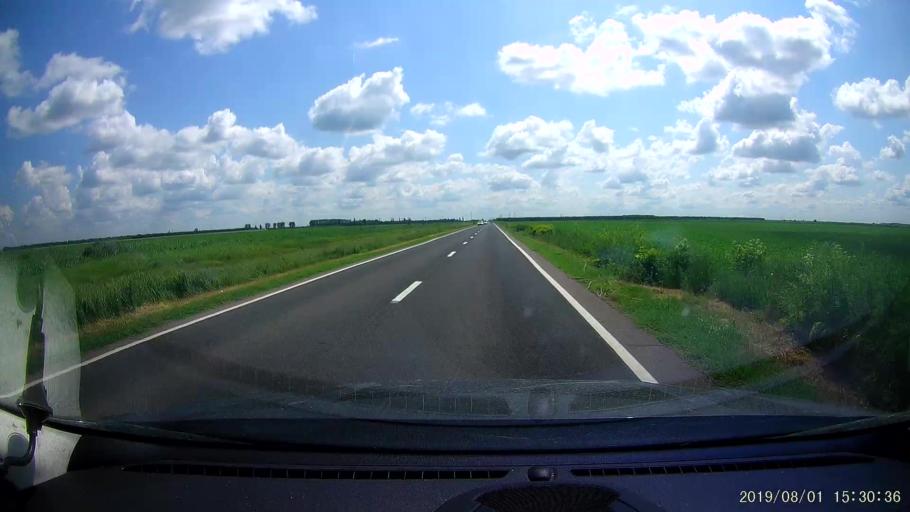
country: RO
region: Braila
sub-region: Comuna Viziru
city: Viziru
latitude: 44.9606
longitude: 27.6745
